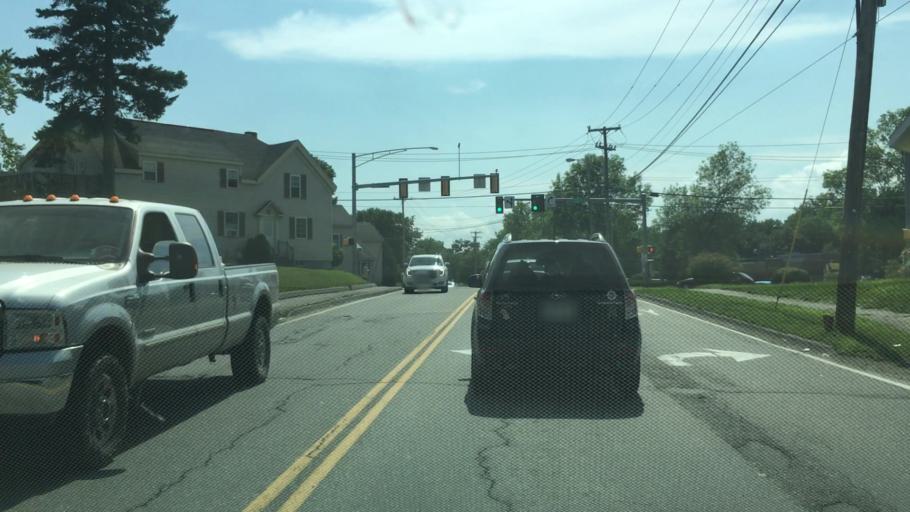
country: US
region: Maine
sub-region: Penobscot County
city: Bangor
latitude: 44.8136
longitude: -68.7677
